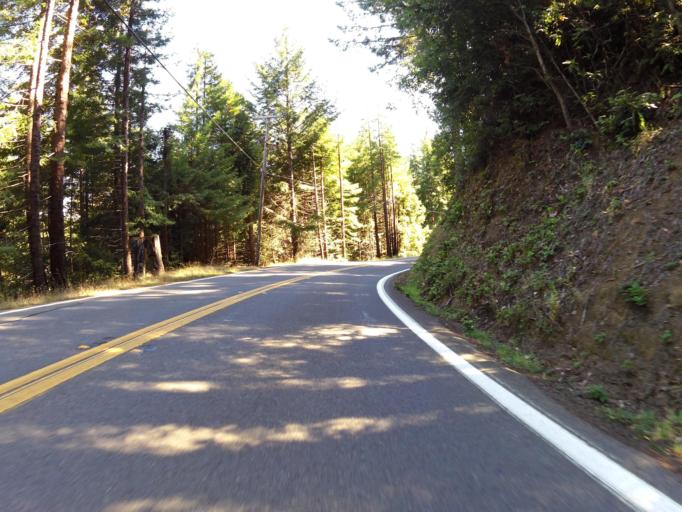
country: US
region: California
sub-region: Mendocino County
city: Fort Bragg
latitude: 39.7228
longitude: -123.8083
